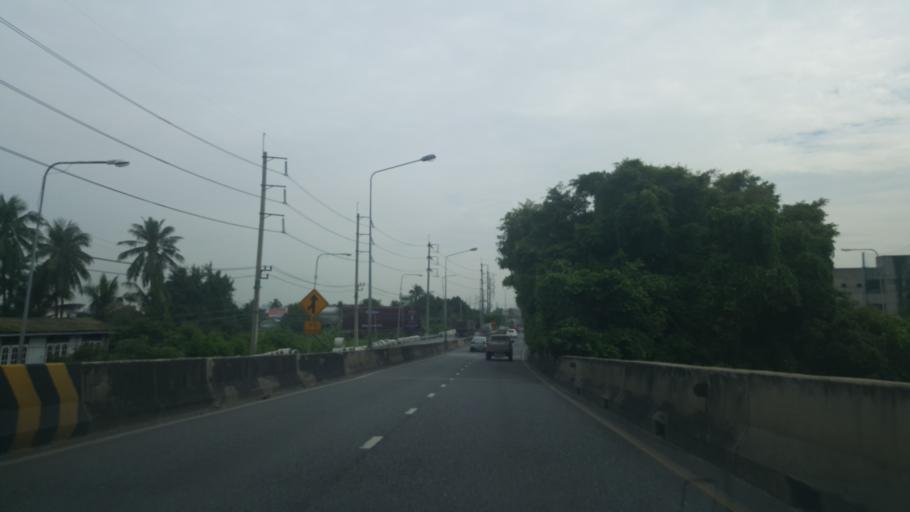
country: TH
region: Bangkok
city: Bang Khae
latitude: 13.6881
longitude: 100.4286
